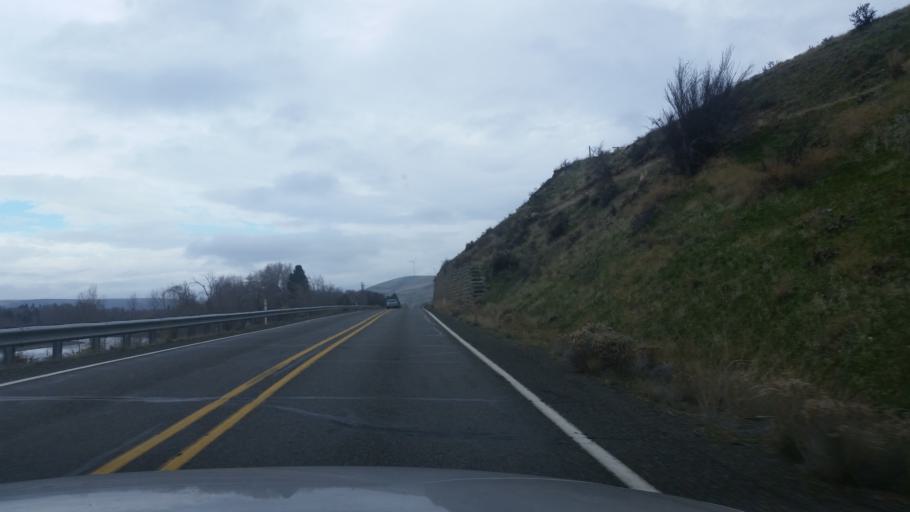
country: US
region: Washington
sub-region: Kittitas County
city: Ellensburg
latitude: 47.0793
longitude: -120.6707
